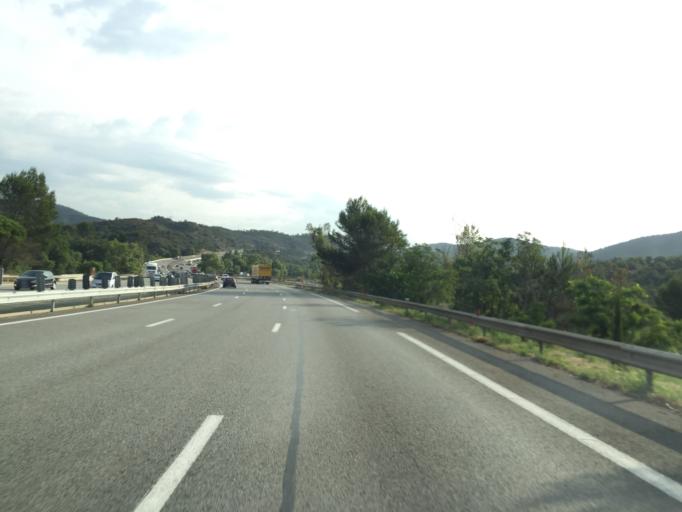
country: FR
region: Provence-Alpes-Cote d'Azur
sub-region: Departement du Var
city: Bagnols-en-Foret
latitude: 43.4987
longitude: 6.7554
